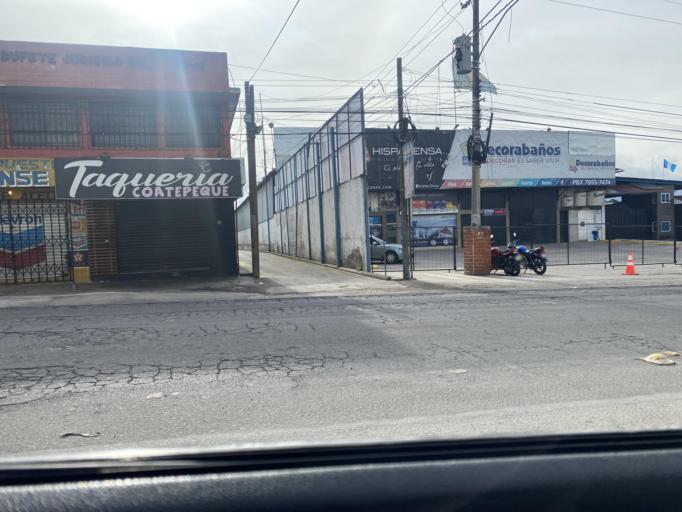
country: GT
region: Quetzaltenango
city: Quetzaltenango
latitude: 14.8573
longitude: -91.5214
